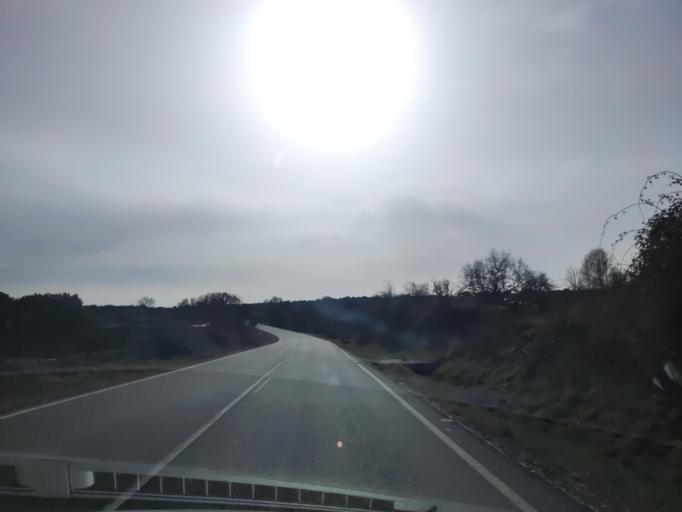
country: ES
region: Castille and Leon
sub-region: Provincia de Salamanca
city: Aldea del Obispo
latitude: 40.7033
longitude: -6.7938
